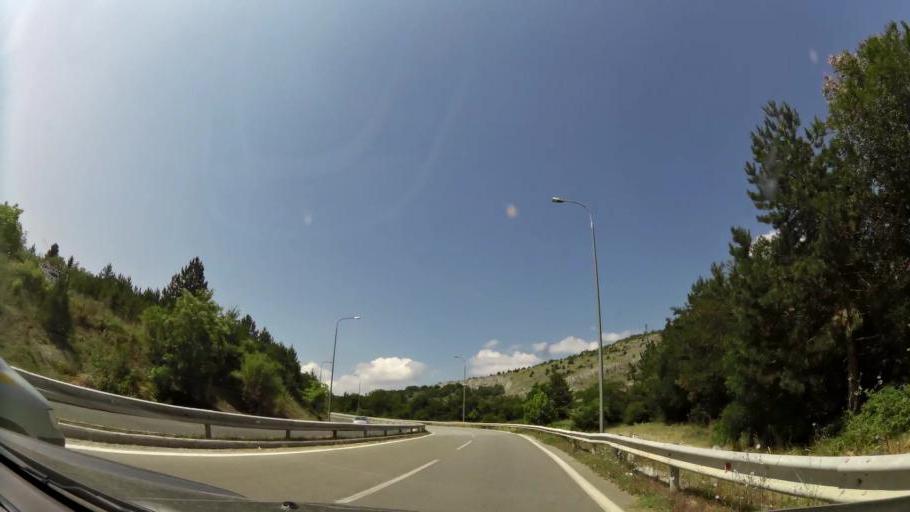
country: GR
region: West Macedonia
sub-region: Nomos Kozanis
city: Kozani
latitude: 40.3155
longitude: 21.7847
